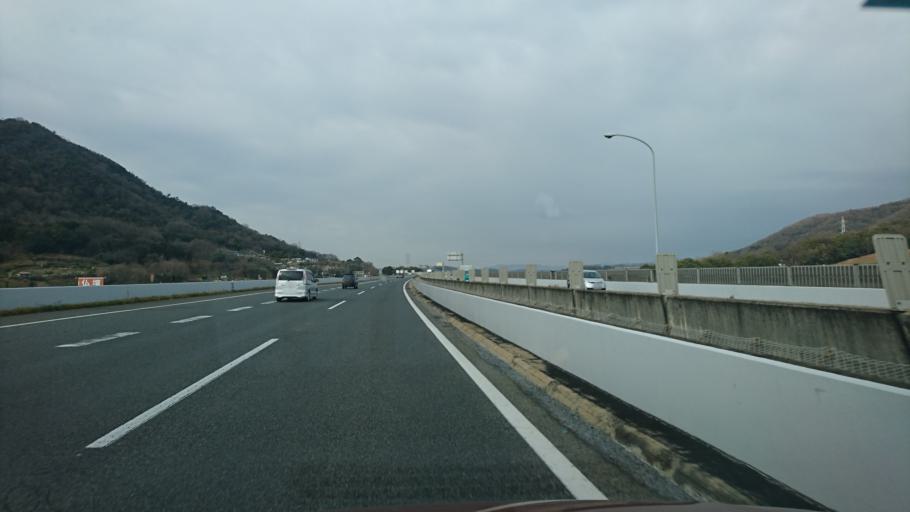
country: JP
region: Hiroshima
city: Fukuyama
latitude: 34.5142
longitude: 133.3932
